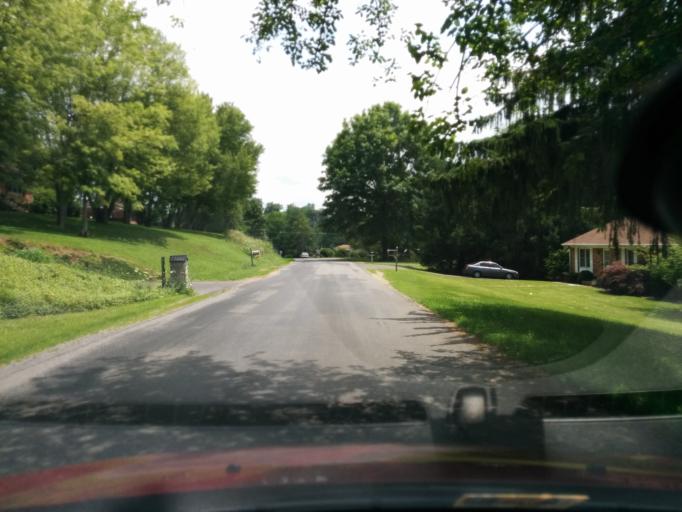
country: US
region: Virginia
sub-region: Rockbridge County
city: East Lexington
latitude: 37.8235
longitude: -79.4006
